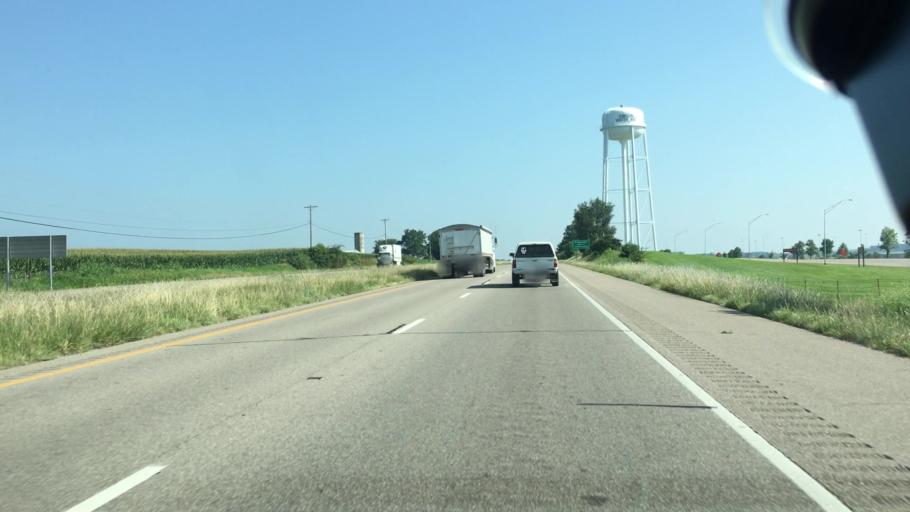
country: US
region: Indiana
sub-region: Gibson County
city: Fort Branch
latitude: 38.2879
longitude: -87.5675
